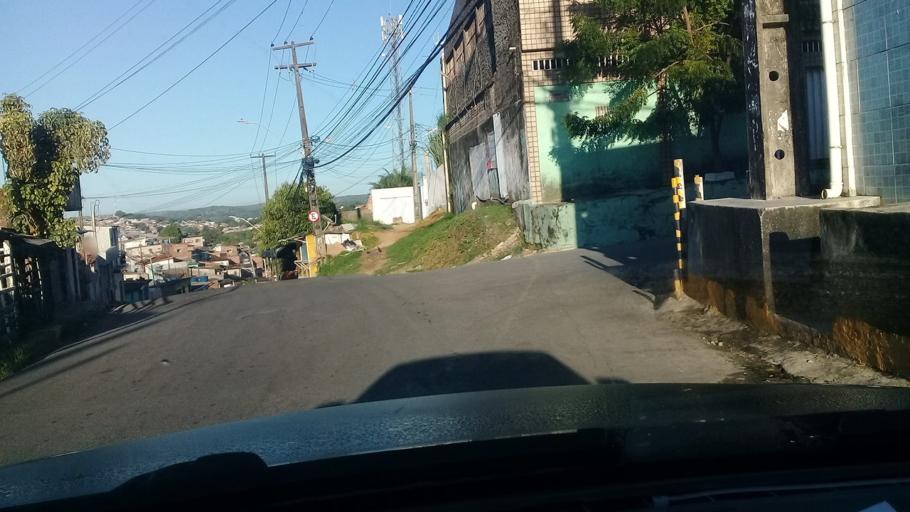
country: BR
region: Pernambuco
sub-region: Jaboatao Dos Guararapes
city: Jaboatao dos Guararapes
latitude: -8.1224
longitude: -34.9547
